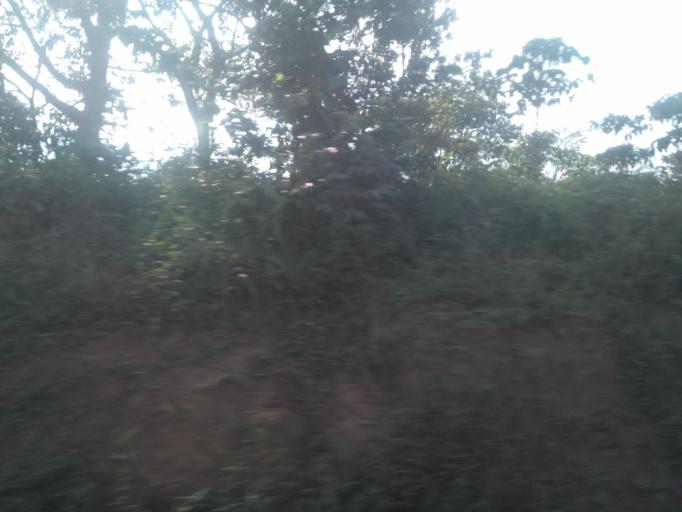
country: UG
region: Central Region
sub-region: Wakiso District
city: Kajansi
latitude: 0.2874
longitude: 32.4550
